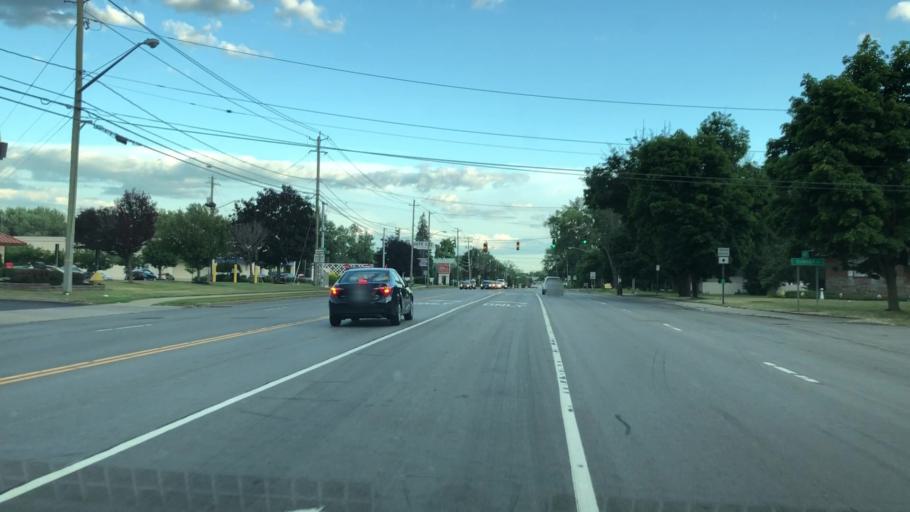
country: US
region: New York
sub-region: Erie County
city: Cheektowaga
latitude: 42.8832
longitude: -78.7543
